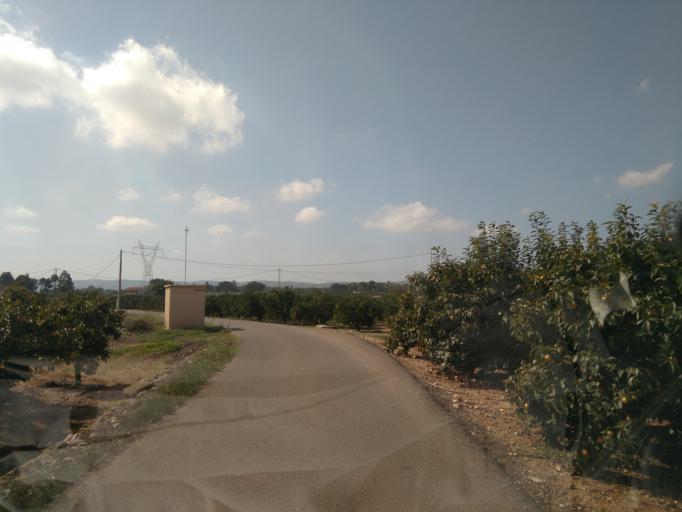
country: ES
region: Valencia
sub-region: Provincia de Valencia
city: Benimodo
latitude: 39.1821
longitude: -0.5479
